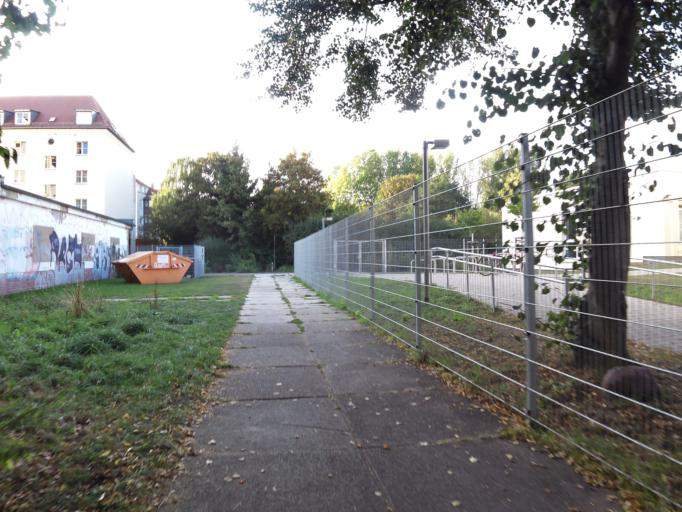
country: DE
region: Saxony
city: Leipzig
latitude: 51.3454
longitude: 12.3219
